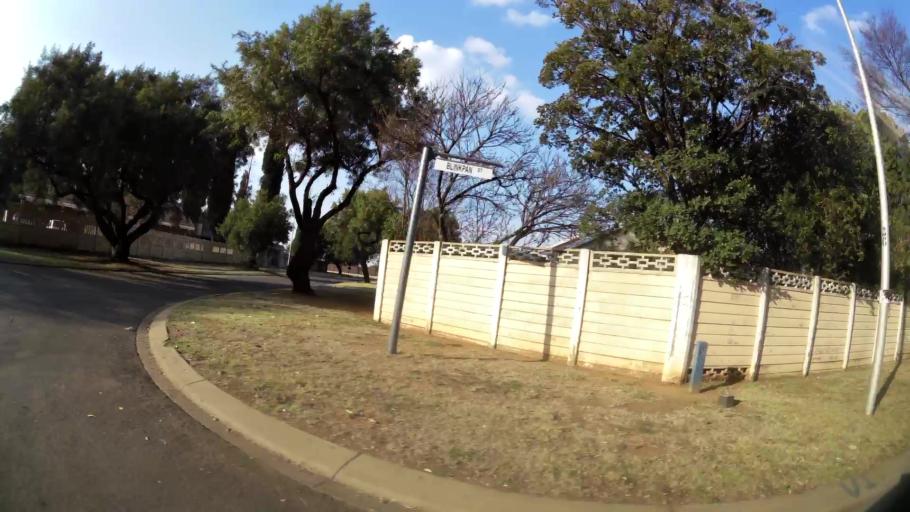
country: ZA
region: Gauteng
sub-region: Ekurhuleni Metropolitan Municipality
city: Benoni
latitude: -26.1296
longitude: 28.3759
